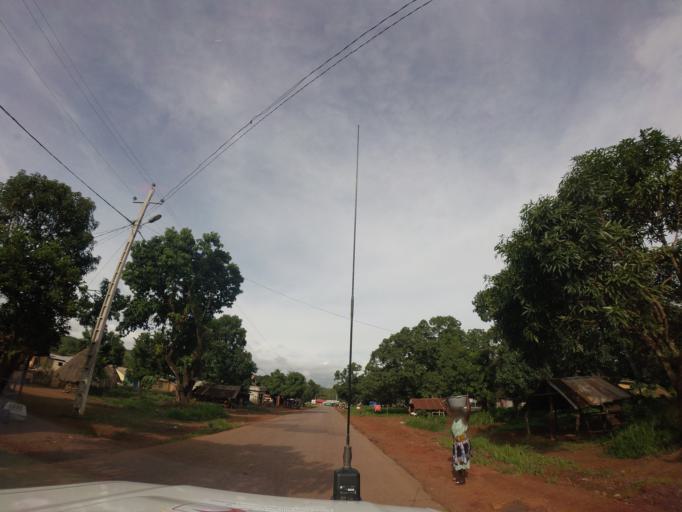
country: GN
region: Kindia
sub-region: Kindia
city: Kindia
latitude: 9.8613
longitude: -13.0804
